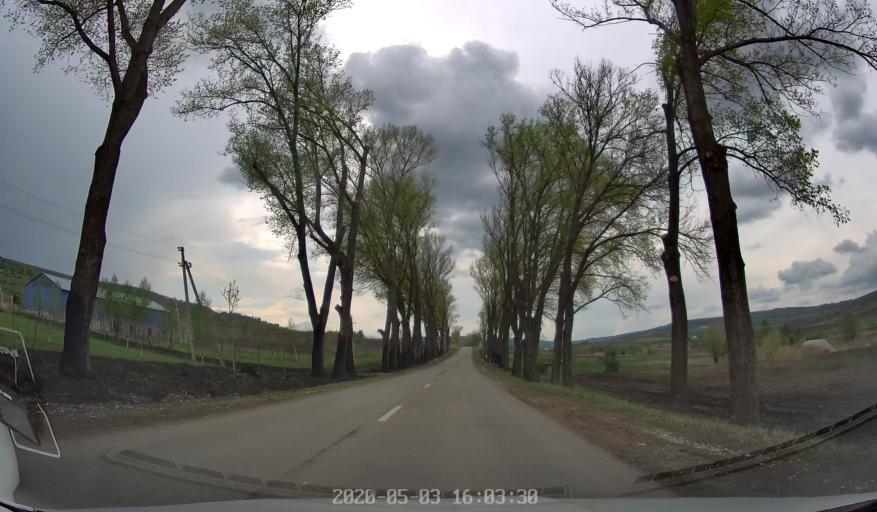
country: MD
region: Stinga Nistrului
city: Bucovat
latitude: 47.1803
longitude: 28.3804
